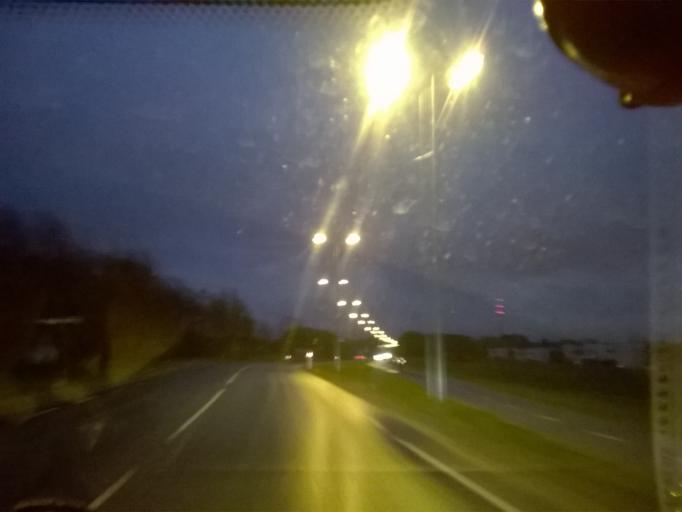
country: EE
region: Harju
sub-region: Viimsi vald
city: Viimsi
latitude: 59.5004
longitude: 24.8701
